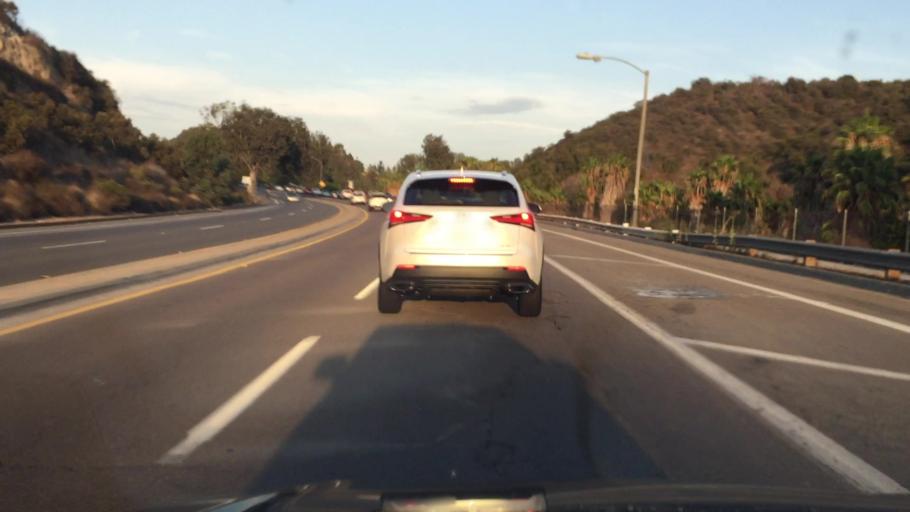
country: US
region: California
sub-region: San Diego County
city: Lemon Grove
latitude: 32.7698
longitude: -117.0910
